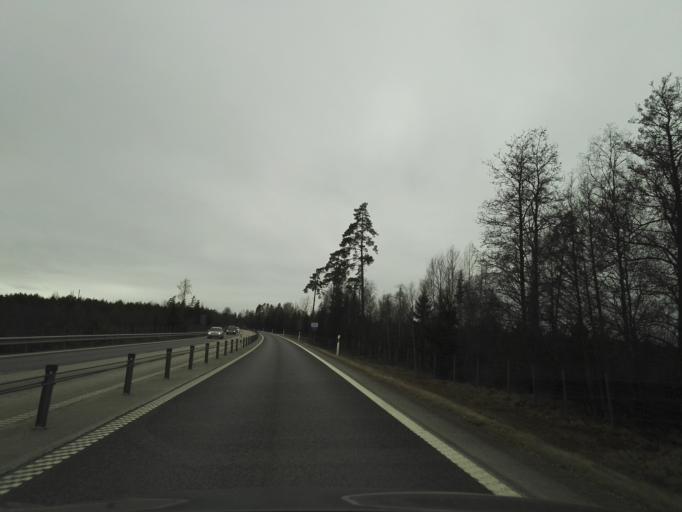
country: SE
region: Kronoberg
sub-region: Vaxjo Kommun
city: Vaexjoe
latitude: 56.8840
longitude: 14.8771
